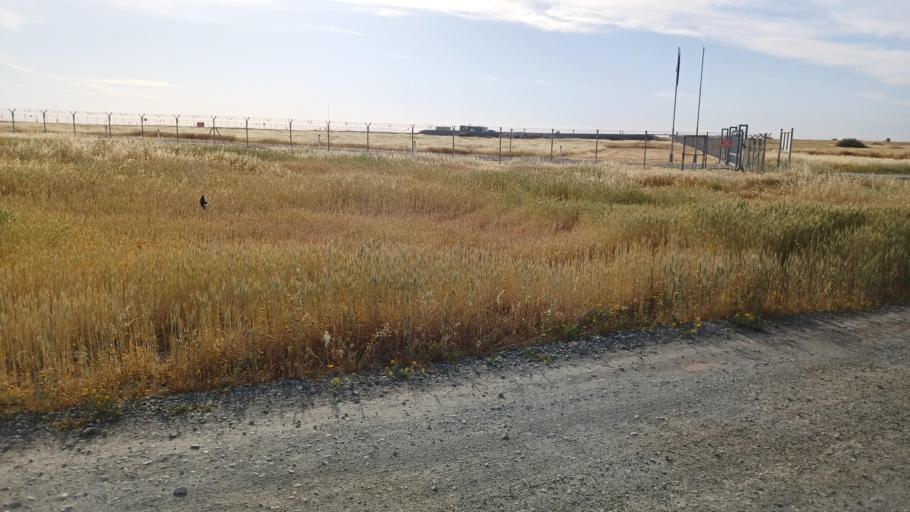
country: CY
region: Lefkosia
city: Mammari
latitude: 35.1724
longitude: 33.2120
